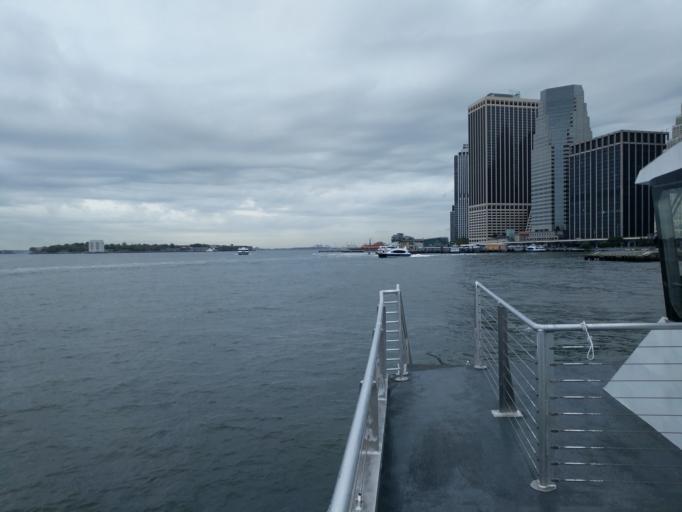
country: US
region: New York
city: New York City
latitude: 40.7042
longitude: -74.0002
